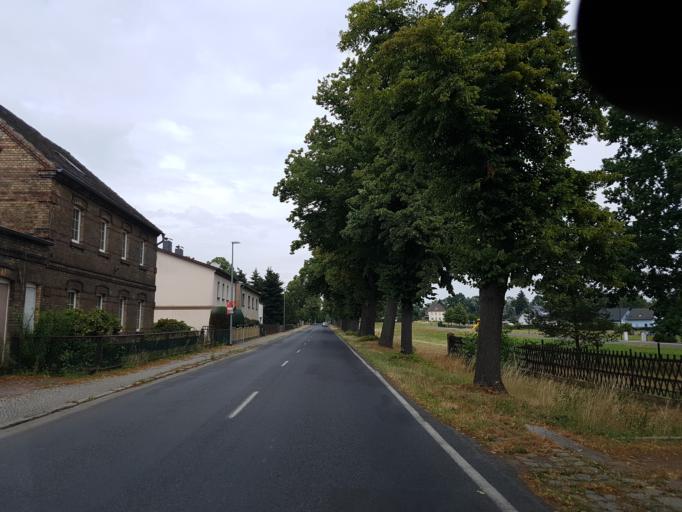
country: DE
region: Brandenburg
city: Schipkau
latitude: 51.5245
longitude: 13.8923
